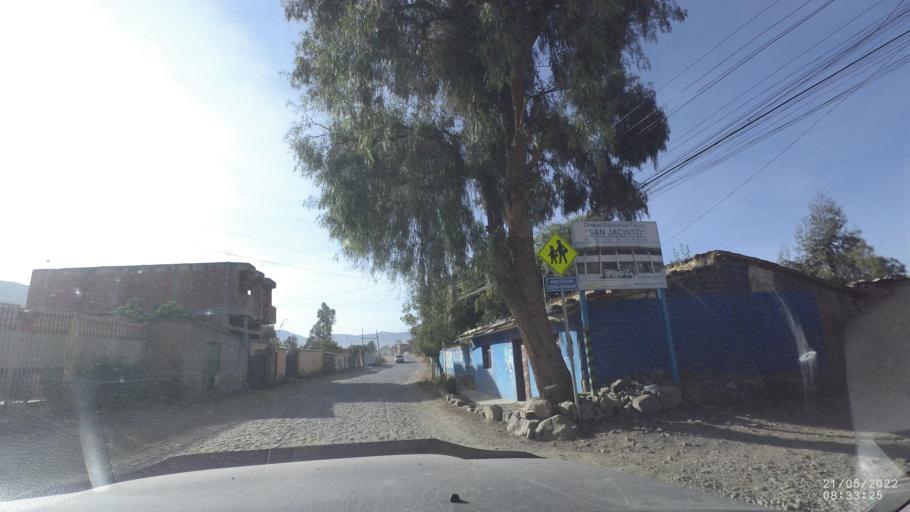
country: BO
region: Cochabamba
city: Cochabamba
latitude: -17.3861
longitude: -66.0505
